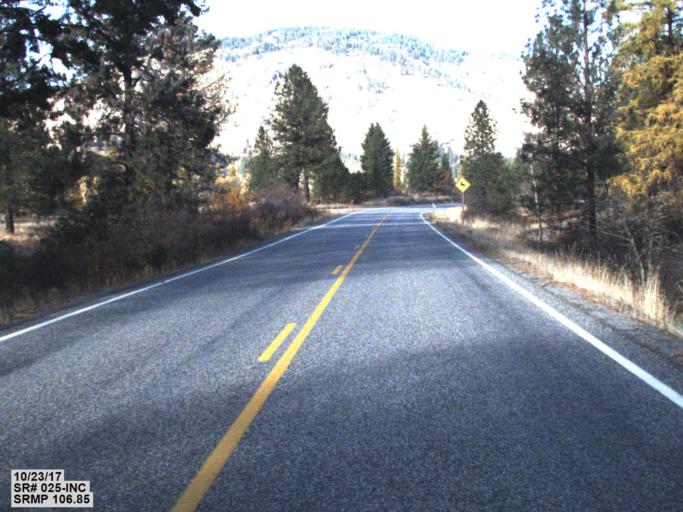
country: CA
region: British Columbia
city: Rossland
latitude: 48.8589
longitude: -117.8780
